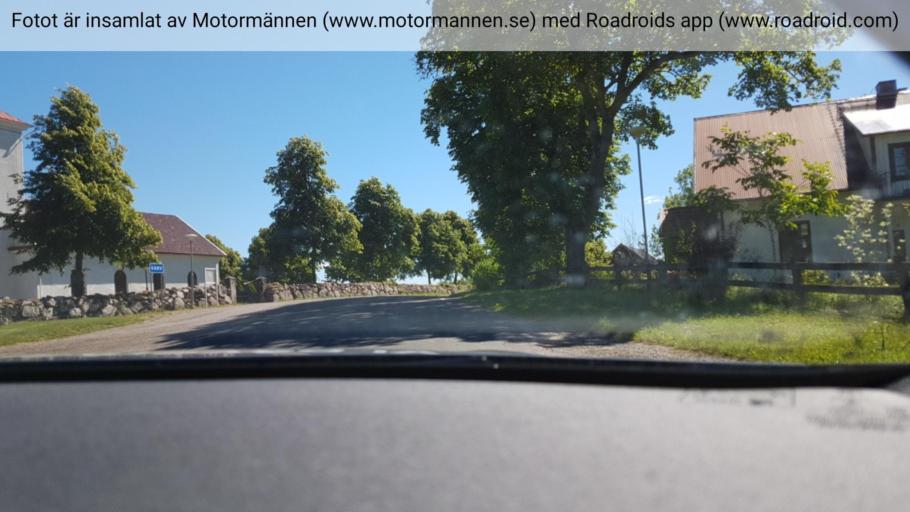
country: SE
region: Vaestra Goetaland
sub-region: Tidaholms Kommun
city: Tidaholm
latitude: 58.1950
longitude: 13.8090
